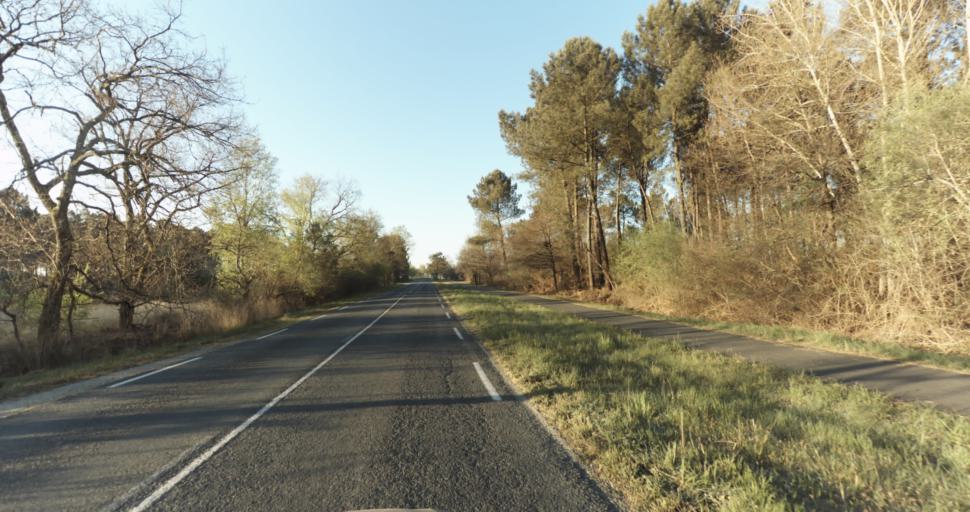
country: FR
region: Aquitaine
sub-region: Departement de la Gironde
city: Martignas-sur-Jalle
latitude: 44.8223
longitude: -0.7785
